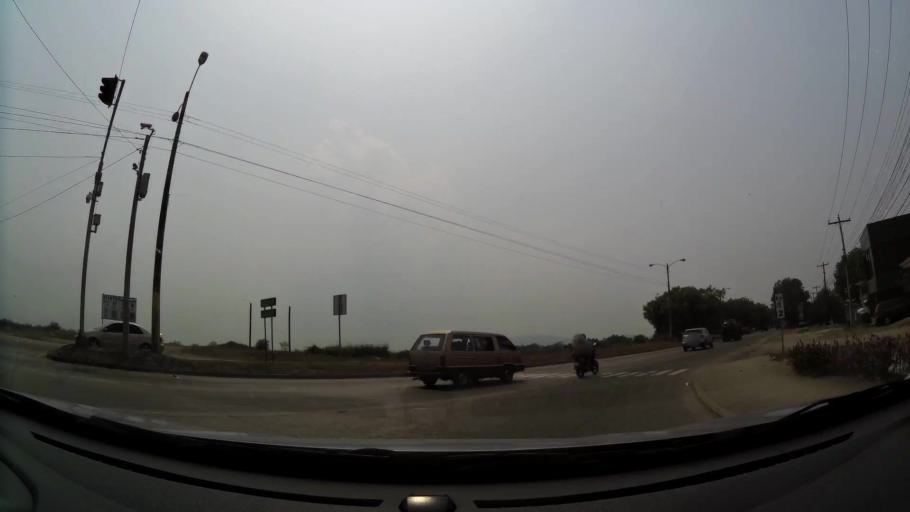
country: HN
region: Cortes
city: La Lima
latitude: 15.4352
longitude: -87.9366
